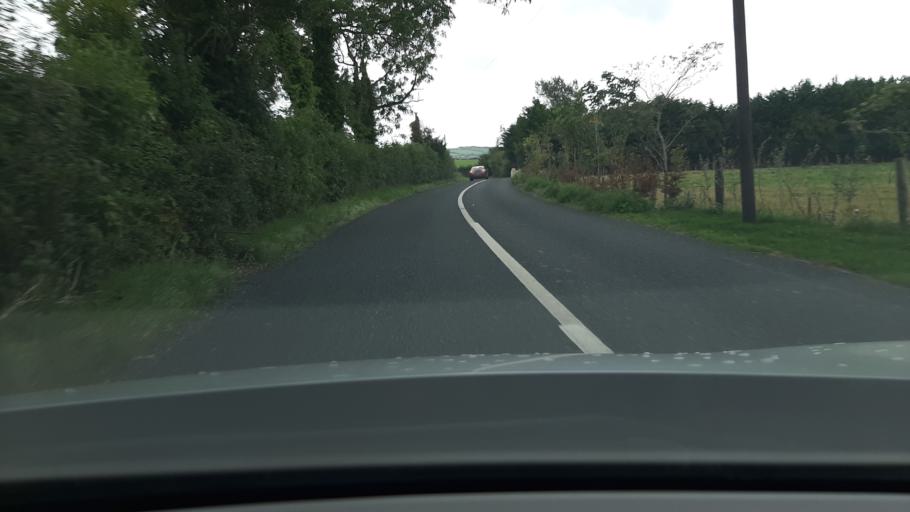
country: IE
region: Leinster
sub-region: Kildare
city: Rathangan
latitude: 53.2099
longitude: -6.9646
